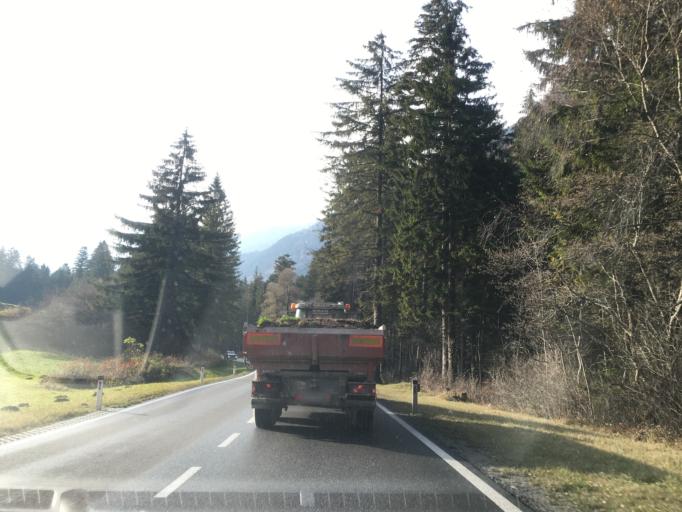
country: AT
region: Vorarlberg
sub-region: Politischer Bezirk Bludenz
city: Stallehr
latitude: 47.1257
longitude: 9.8580
